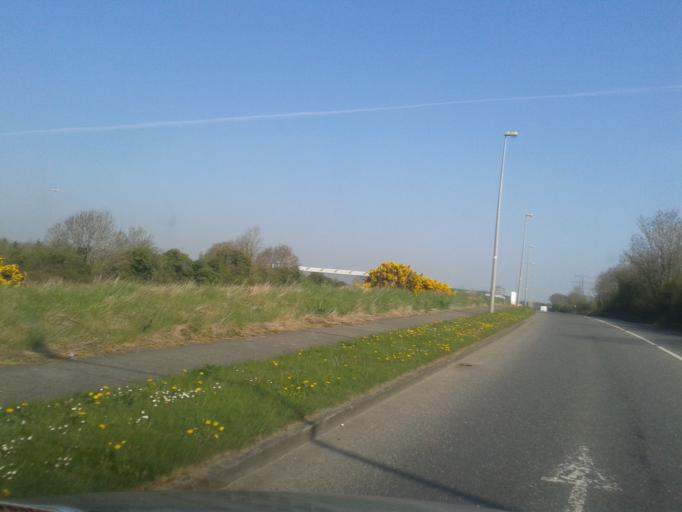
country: IE
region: Leinster
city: Balrothery
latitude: 53.5653
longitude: -6.2095
